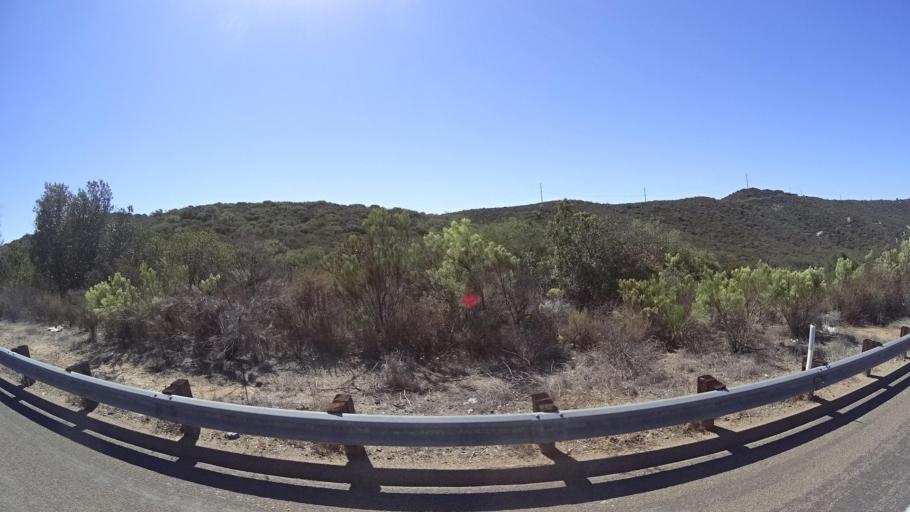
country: US
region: California
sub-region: San Diego County
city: Alpine
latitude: 32.8029
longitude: -116.7727
